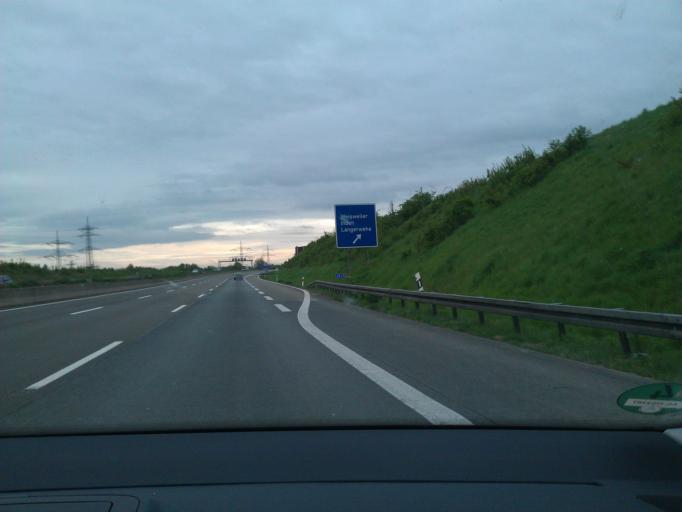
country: DE
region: North Rhine-Westphalia
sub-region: Regierungsbezirk Koln
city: Langerwehe
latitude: 50.8319
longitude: 6.3161
